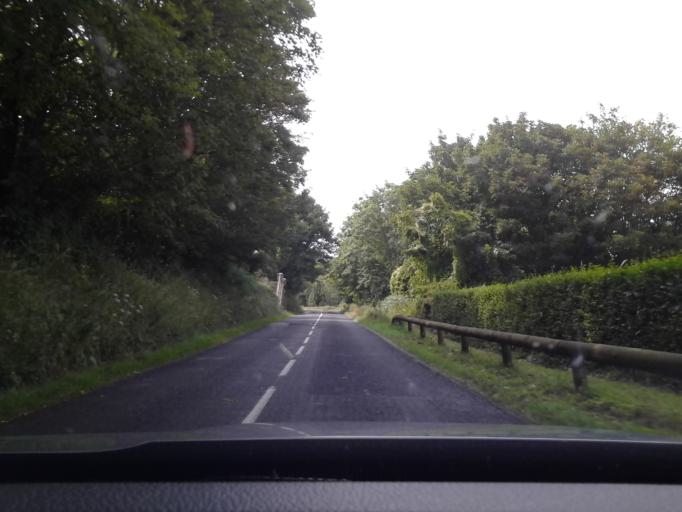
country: FR
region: Lower Normandy
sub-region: Departement de la Manche
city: Urville-Nacqueville
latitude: 49.6787
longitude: -1.7661
